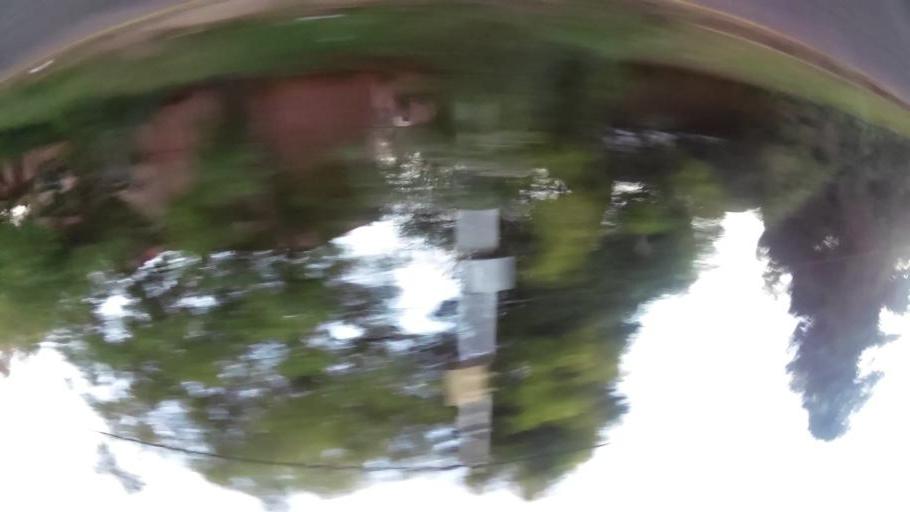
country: ZA
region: Gauteng
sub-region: City of Johannesburg Metropolitan Municipality
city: Roodepoort
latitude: -26.1702
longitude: 27.9103
